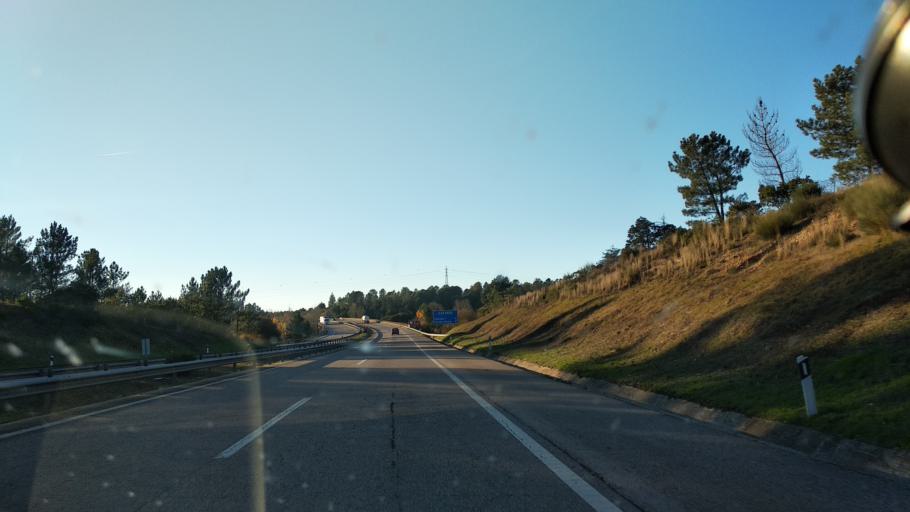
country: PT
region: Santarem
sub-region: Entroncamento
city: Entroncamento
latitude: 39.4895
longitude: -8.4526
